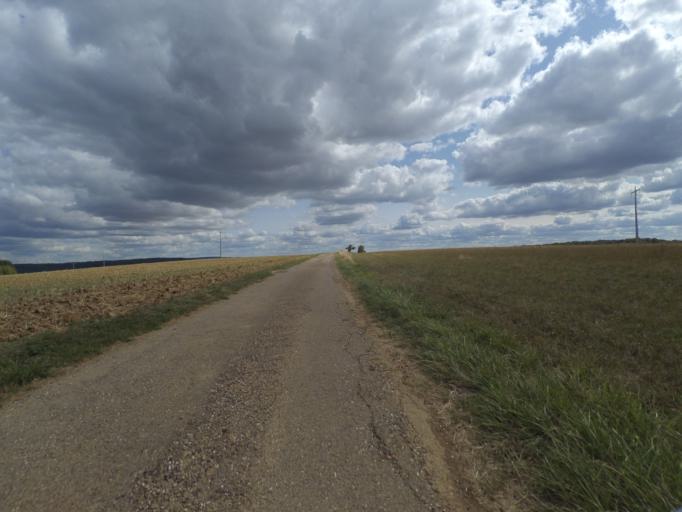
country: LU
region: Grevenmacher
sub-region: Canton de Remich
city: Mondorf-les-Bains
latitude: 49.5299
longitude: 6.2848
